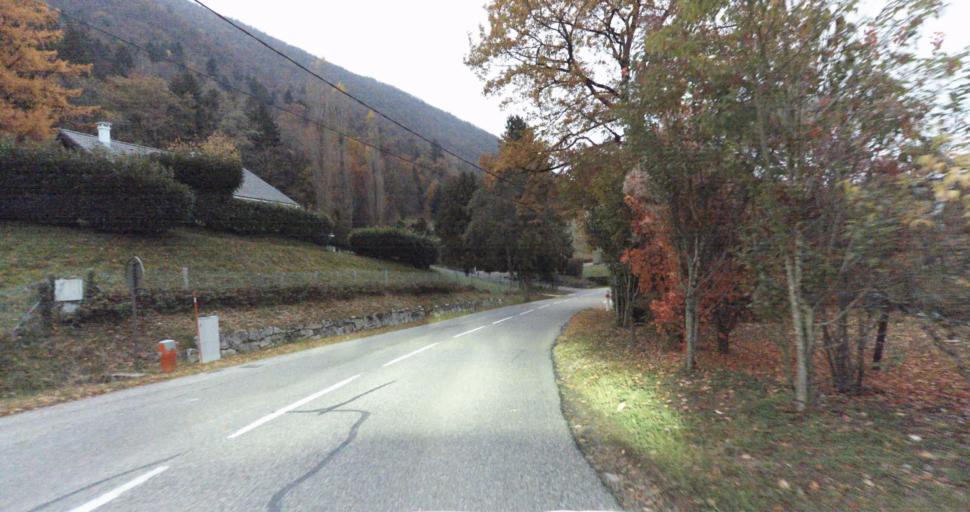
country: FR
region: Rhone-Alpes
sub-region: Departement de la Haute-Savoie
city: Sevrier
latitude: 45.8498
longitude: 6.1373
